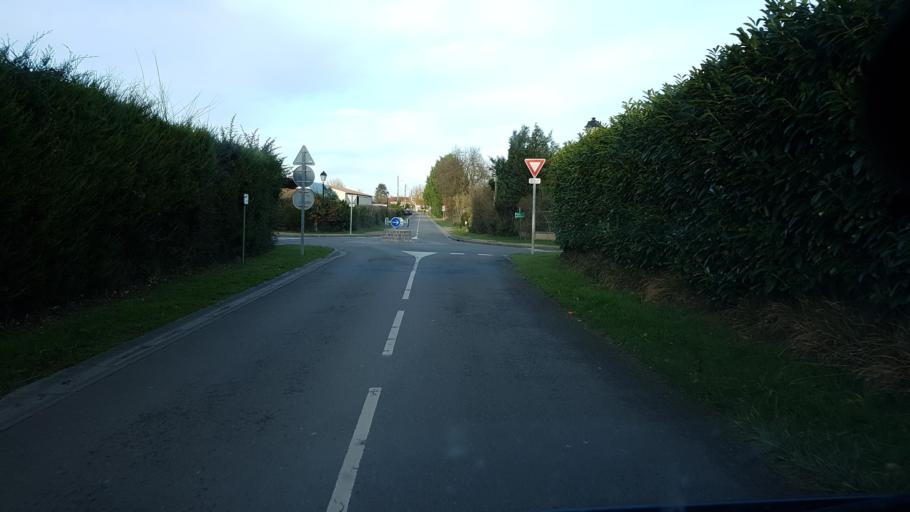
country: FR
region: Ile-de-France
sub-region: Departement des Yvelines
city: Le Perray-en-Yvelines
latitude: 48.7005
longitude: 1.8091
